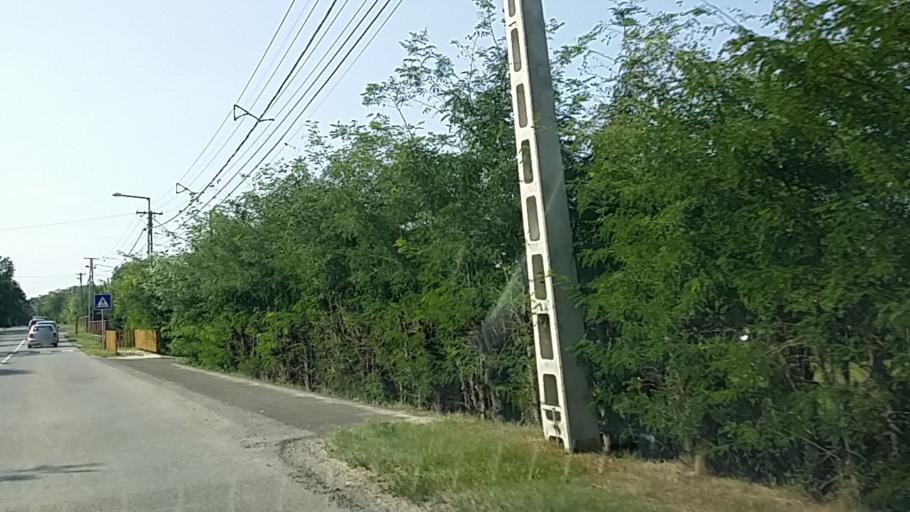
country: HU
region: Pest
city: Erdokertes
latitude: 47.6703
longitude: 19.3273
